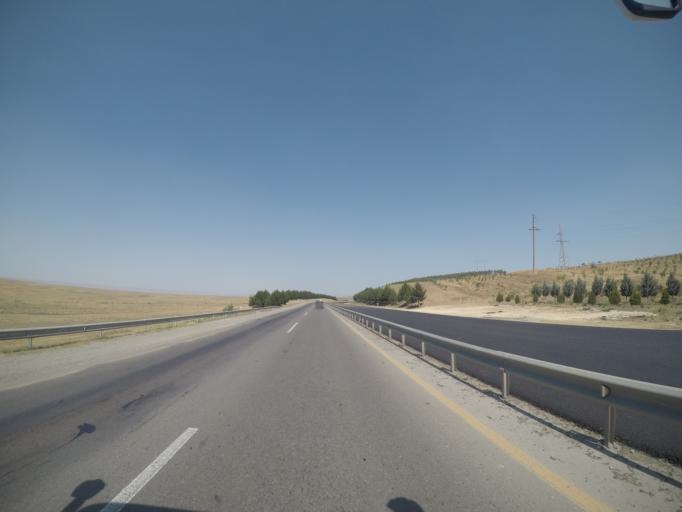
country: AZ
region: Haciqabul
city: Haciqabul
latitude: 40.0469
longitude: 48.9827
